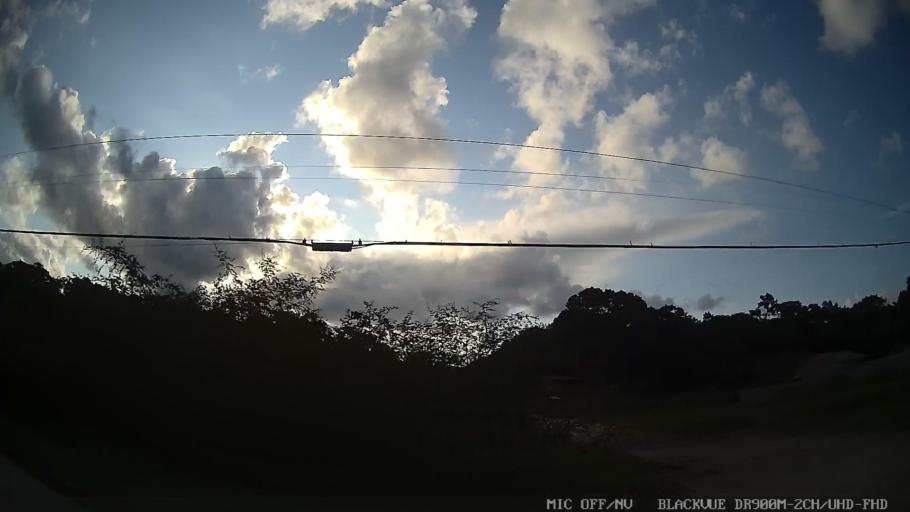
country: BR
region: Sao Paulo
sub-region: Itanhaem
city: Itanhaem
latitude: -24.1578
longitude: -46.8287
